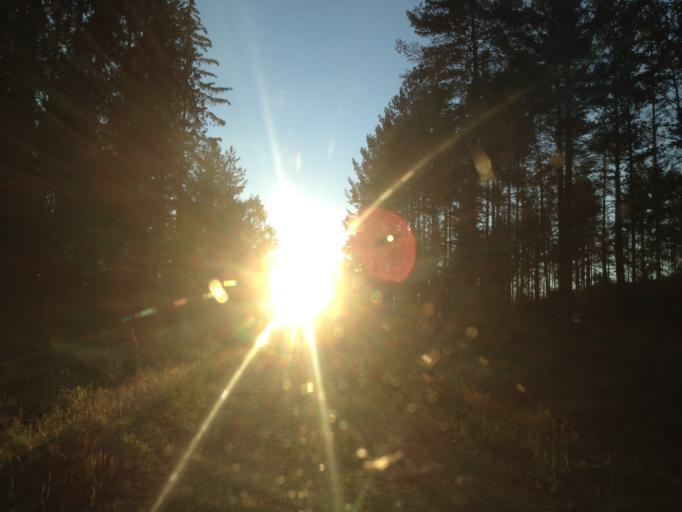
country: SE
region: Kalmar
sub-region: Vasterviks Kommun
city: Overum
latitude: 57.9995
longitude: 16.1325
